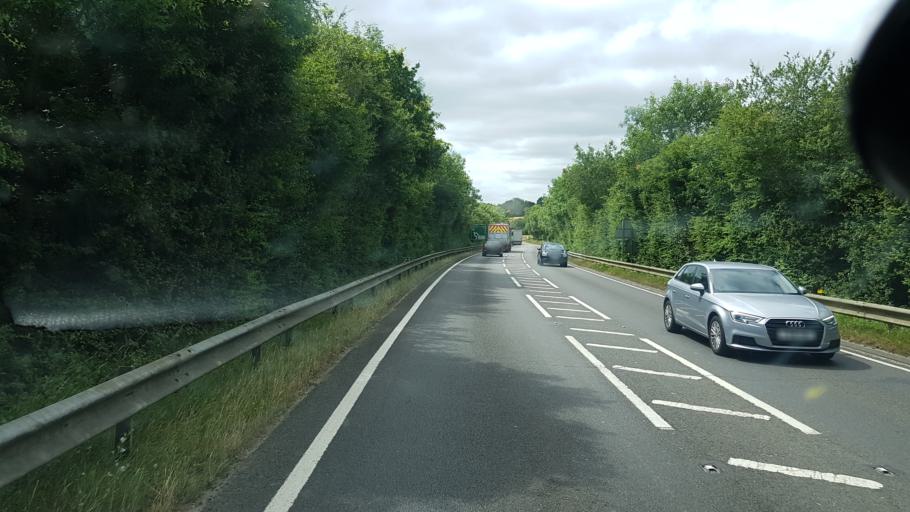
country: GB
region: England
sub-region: Surrey
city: Godstone
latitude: 51.2377
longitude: -0.0476
